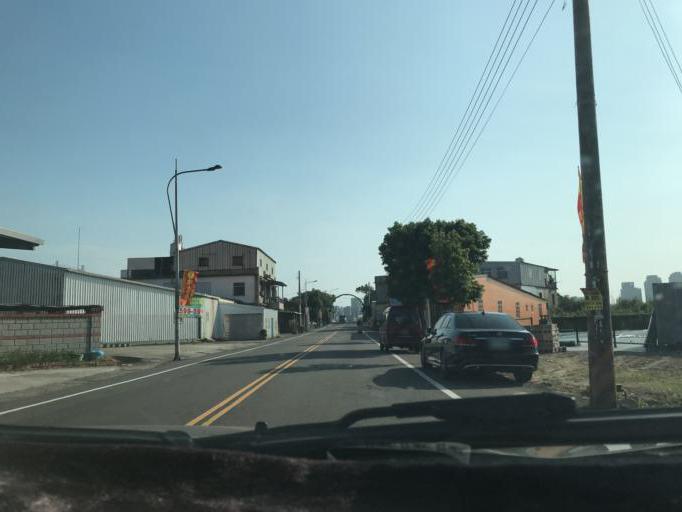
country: TW
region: Taiwan
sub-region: Hsinchu
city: Zhubei
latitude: 24.8403
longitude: 121.0365
